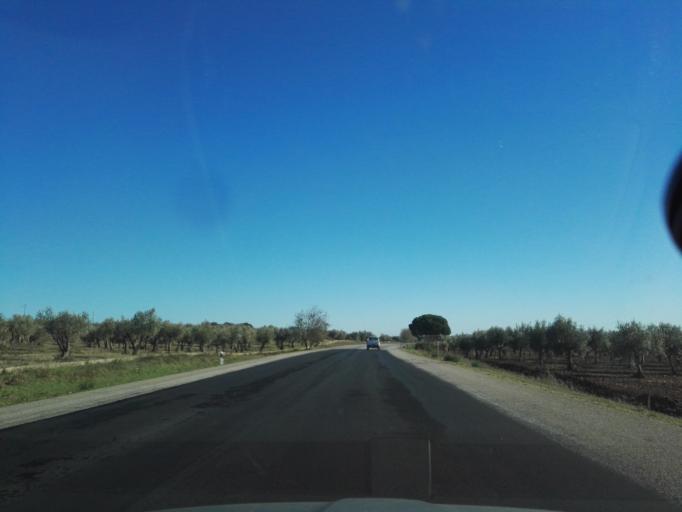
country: PT
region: Evora
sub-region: Estremoz
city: Estremoz
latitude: 38.8311
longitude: -7.5364
